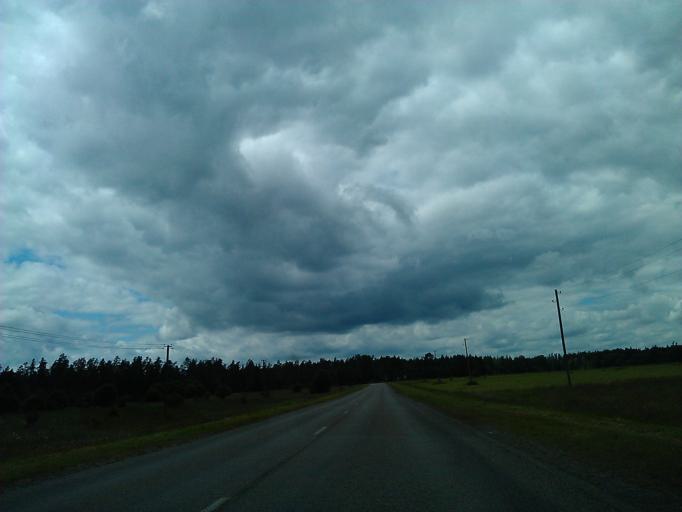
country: LV
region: Talsu Rajons
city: Stende
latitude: 57.0871
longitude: 22.3159
